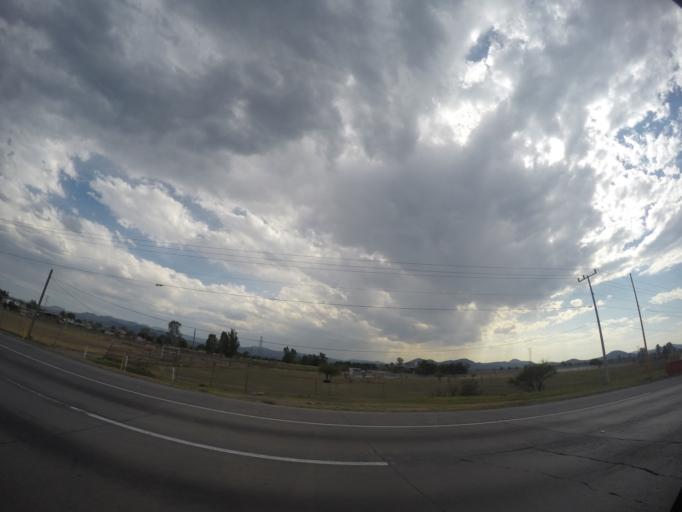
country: MX
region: Queretaro
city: La Estancia
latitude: 20.4111
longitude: -100.0387
